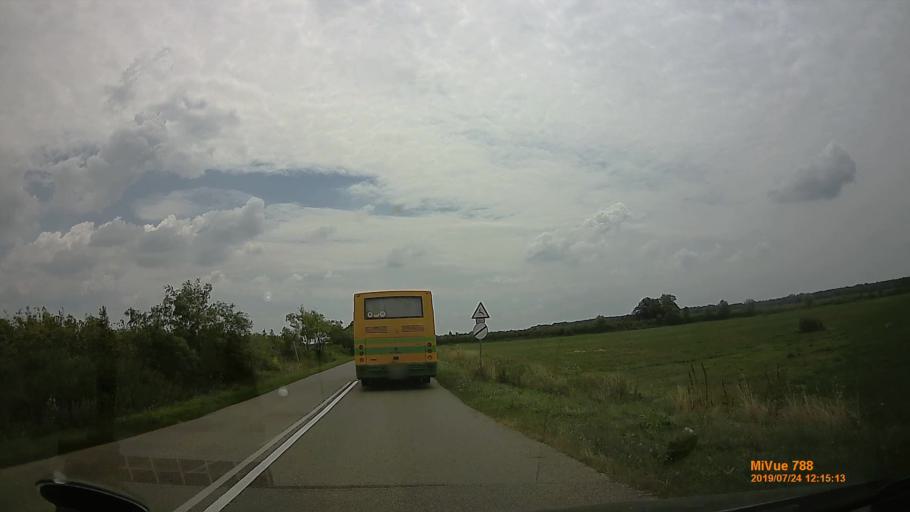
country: HU
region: Szabolcs-Szatmar-Bereg
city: Vasarosnameny
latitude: 48.1868
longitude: 22.3443
